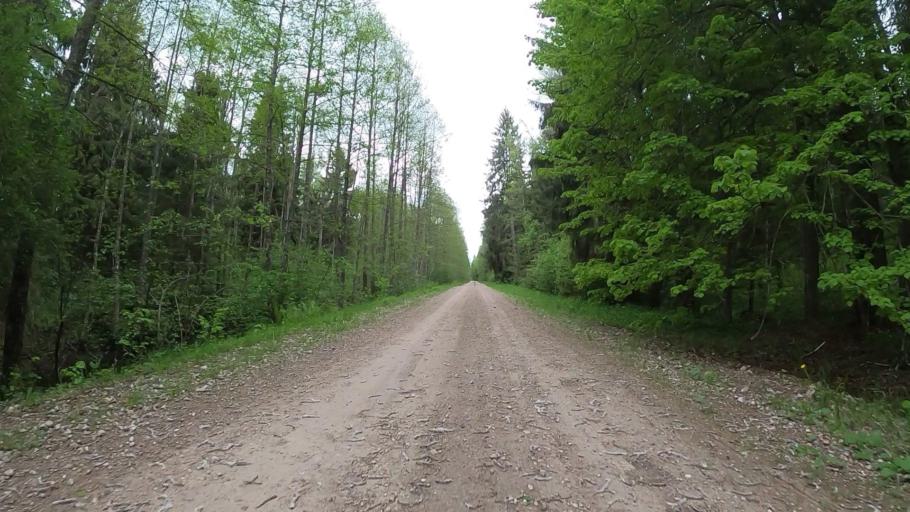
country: LV
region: Ozolnieku
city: Ozolnieki
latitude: 56.8081
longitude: 23.7867
